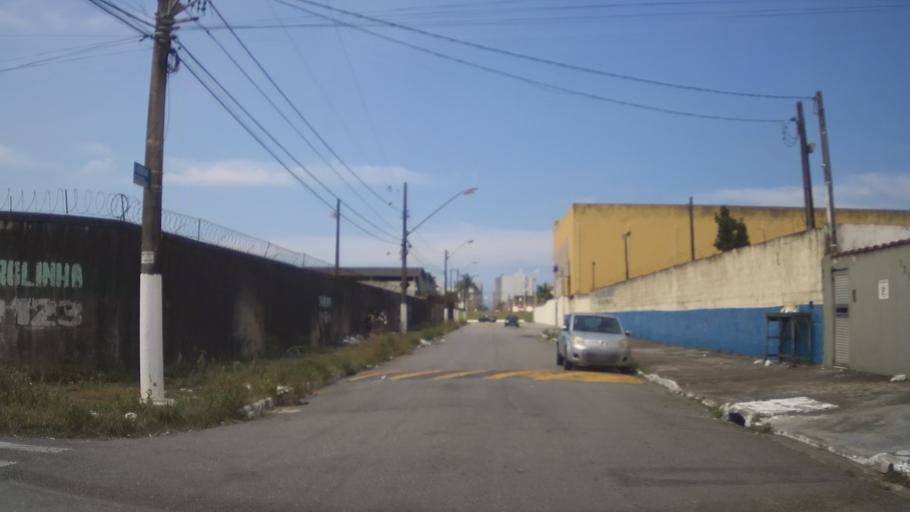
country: BR
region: Sao Paulo
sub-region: Praia Grande
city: Praia Grande
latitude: -24.0221
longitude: -46.4880
